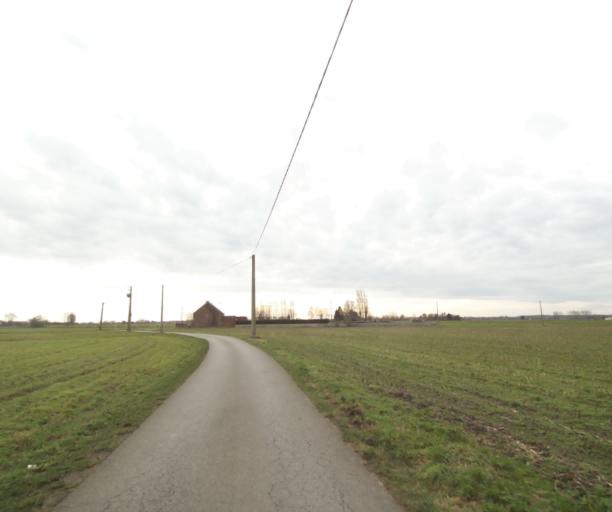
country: FR
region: Nord-Pas-de-Calais
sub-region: Departement du Nord
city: Hergnies
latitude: 50.4876
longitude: 3.5481
